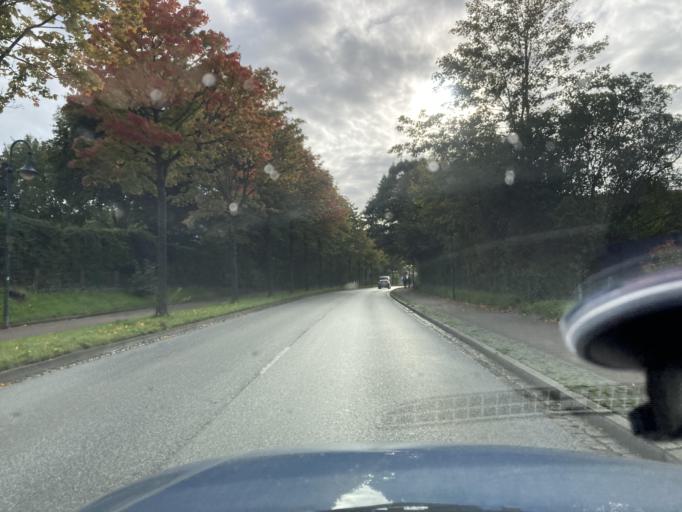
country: DE
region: Schleswig-Holstein
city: Budelsdorf
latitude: 54.3179
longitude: 9.6855
